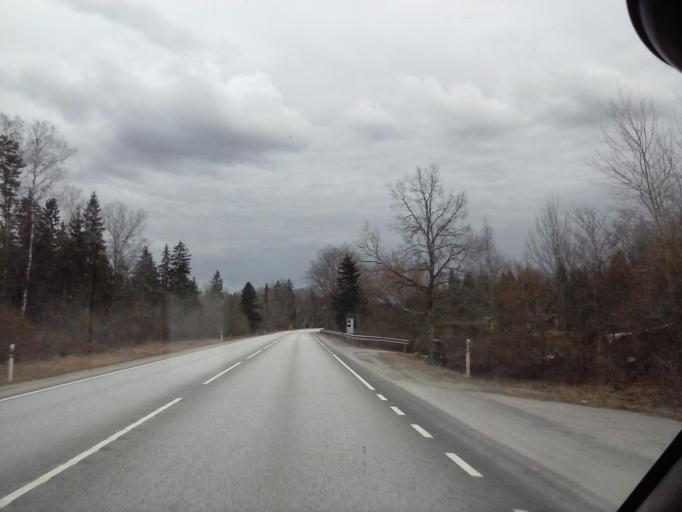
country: EE
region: Jaervamaa
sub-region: Paide linn
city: Paide
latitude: 59.0283
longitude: 25.5803
